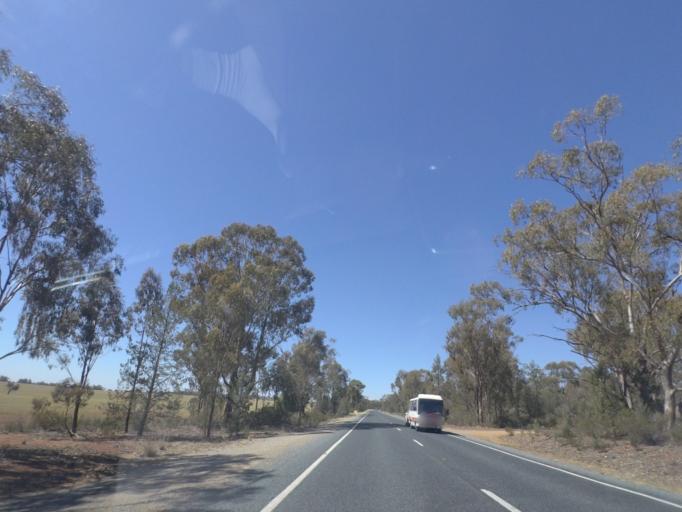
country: AU
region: New South Wales
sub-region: Narrandera
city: Narrandera
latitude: -34.4361
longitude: 146.8422
